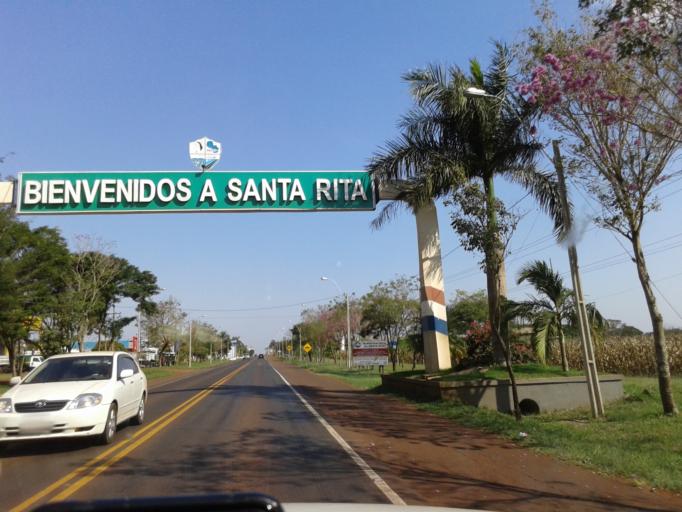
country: PY
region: Alto Parana
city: Santa Rita
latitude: -25.7471
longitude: -55.0537
